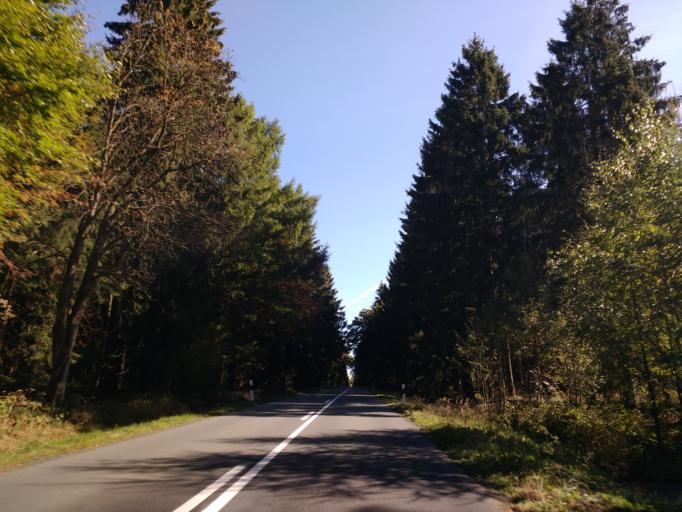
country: DE
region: North Rhine-Westphalia
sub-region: Regierungsbezirk Detmold
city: Willebadessen
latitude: 51.6213
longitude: 8.9727
